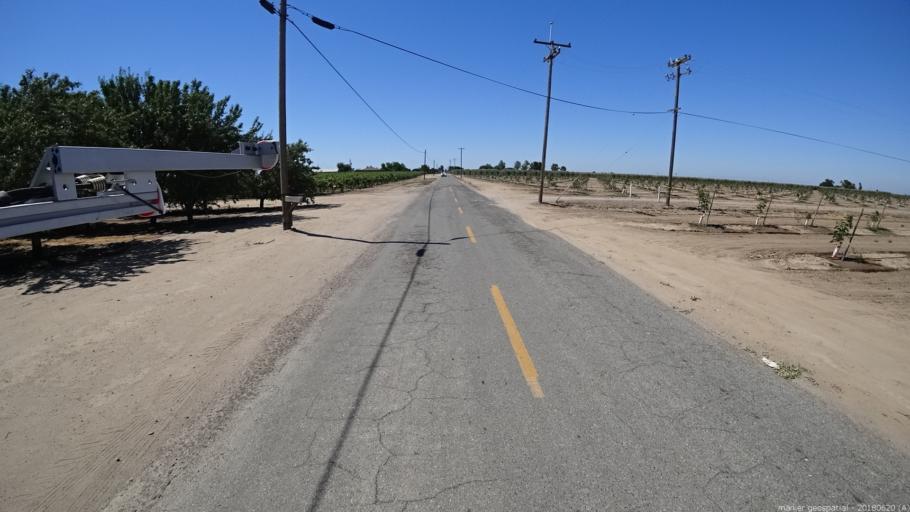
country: US
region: California
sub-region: Madera County
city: Parkwood
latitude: 36.8751
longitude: -120.0104
